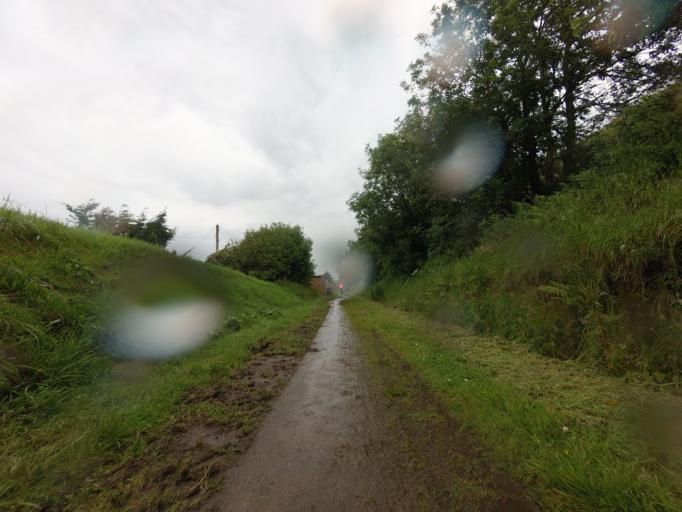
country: GB
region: Scotland
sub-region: Moray
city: Buckie
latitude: 57.6643
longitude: -3.0095
